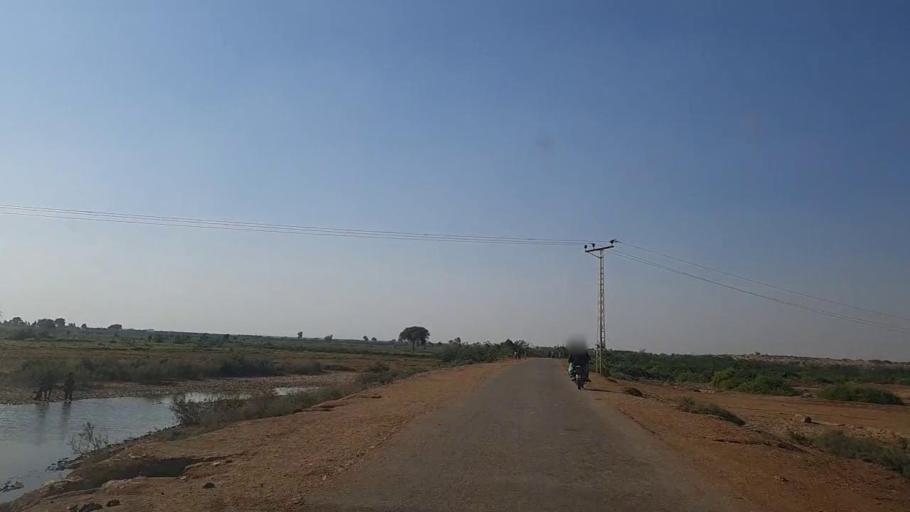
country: PK
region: Sindh
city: Daro Mehar
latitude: 24.9858
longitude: 68.1338
